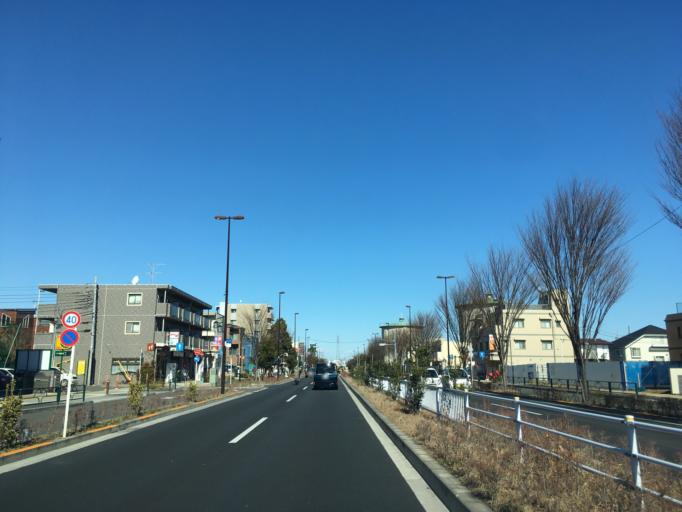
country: JP
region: Tokyo
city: Mitaka-shi
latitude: 35.6850
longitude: 139.5498
